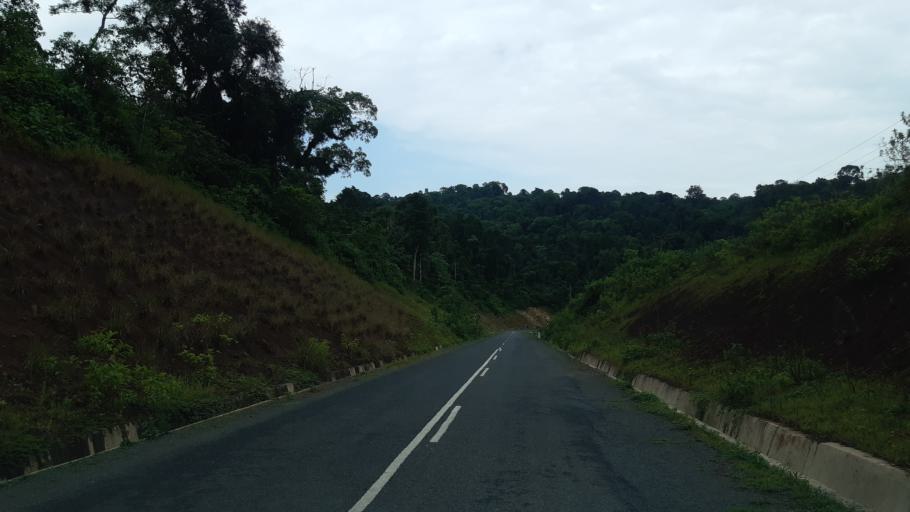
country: ET
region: Southern Nations, Nationalities, and People's Region
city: Bonga
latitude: 7.2030
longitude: 36.2809
